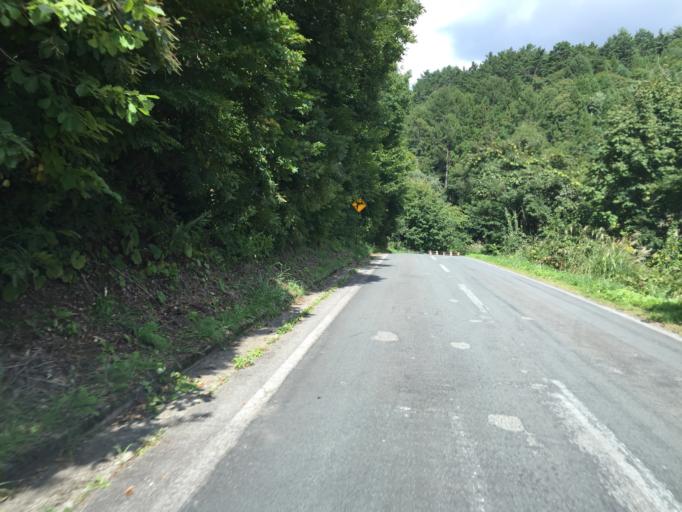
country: JP
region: Fukushima
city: Inawashiro
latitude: 37.5911
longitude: 140.0308
